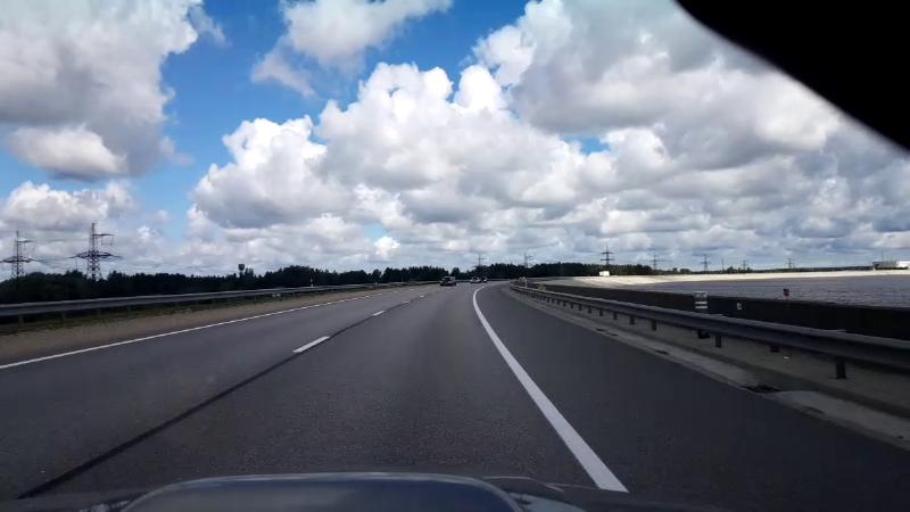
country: LV
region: Kekava
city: Kekava
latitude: 56.8440
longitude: 24.2649
